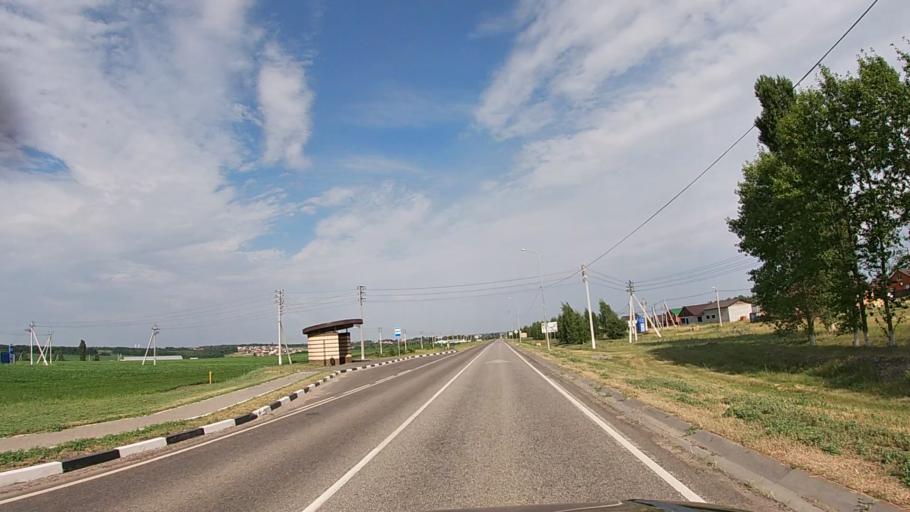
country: RU
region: Belgorod
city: Krasnaya Yaruga
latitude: 50.7965
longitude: 35.6914
